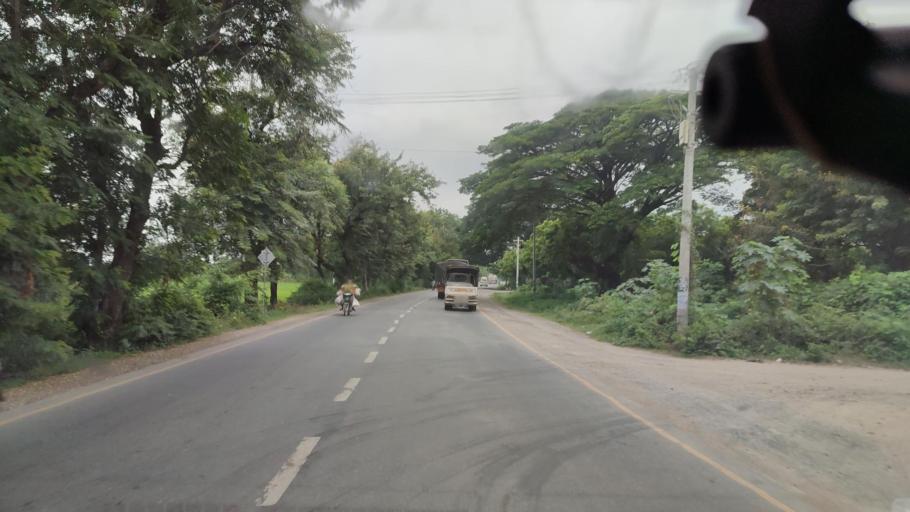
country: MM
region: Mandalay
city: Mandalay
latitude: 22.2096
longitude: 96.1328
